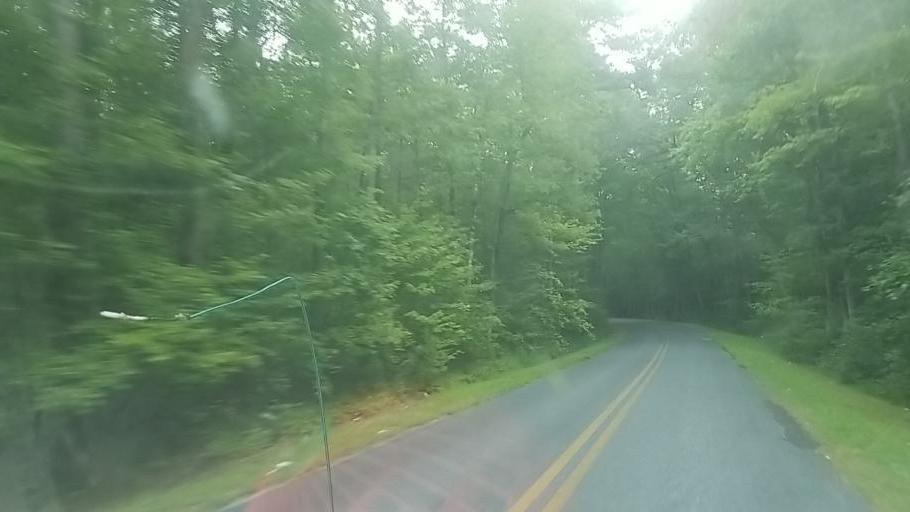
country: US
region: Maryland
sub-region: Wicomico County
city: Pittsville
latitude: 38.4145
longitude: -75.4779
